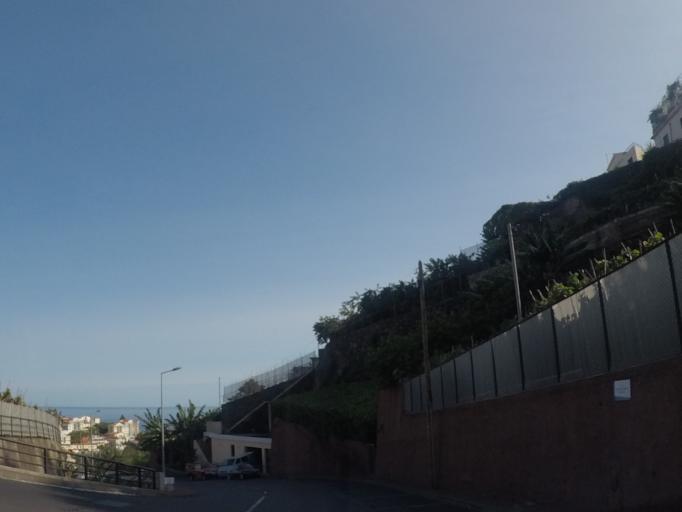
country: PT
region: Madeira
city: Camara de Lobos
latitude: 32.6546
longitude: -16.9868
